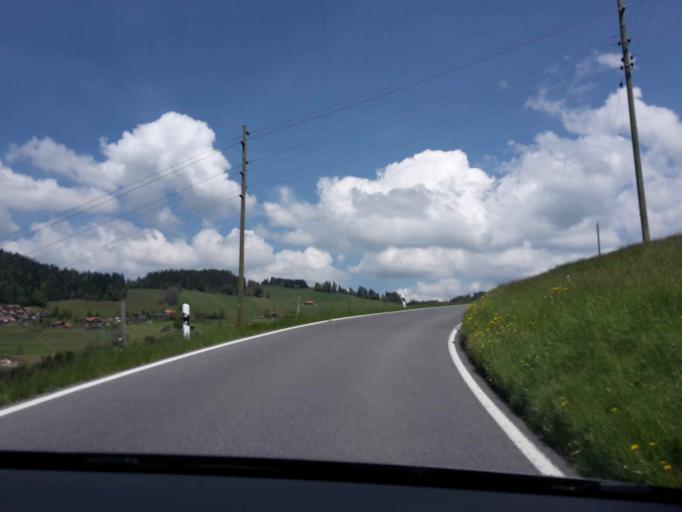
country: CH
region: Bern
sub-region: Thun District
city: Hilterfingen
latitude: 46.7547
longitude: 7.6735
